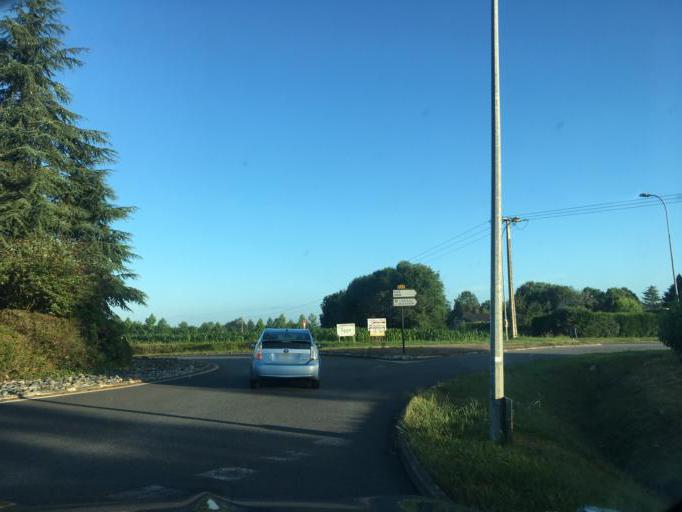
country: FR
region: Aquitaine
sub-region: Departement des Pyrenees-Atlantiques
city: Ger
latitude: 43.2482
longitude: -0.0567
